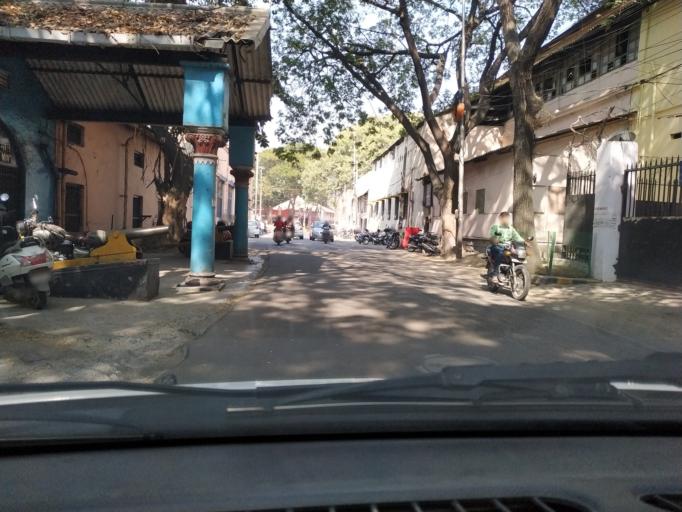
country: IN
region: Telangana
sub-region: Hyderabad
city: Hyderabad
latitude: 17.4097
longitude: 78.4675
